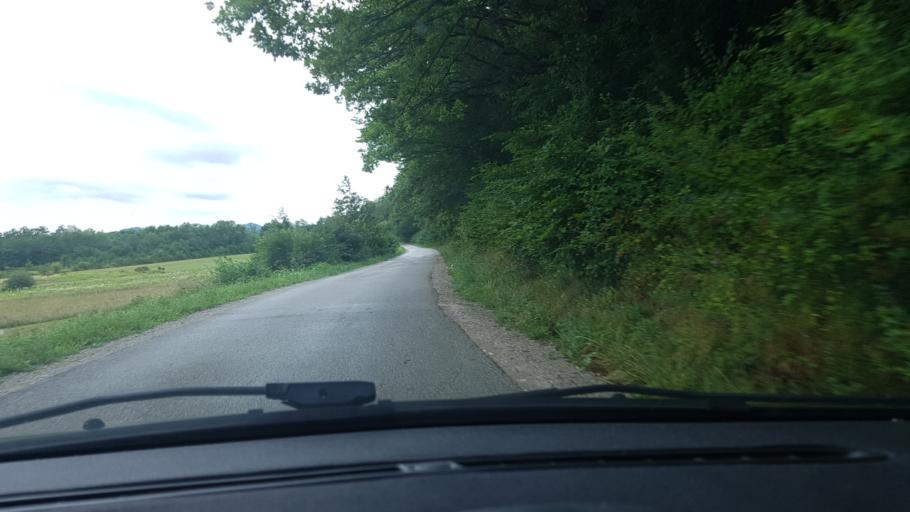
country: HR
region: Karlovacka
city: Ozalj
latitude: 45.6139
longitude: 15.5282
